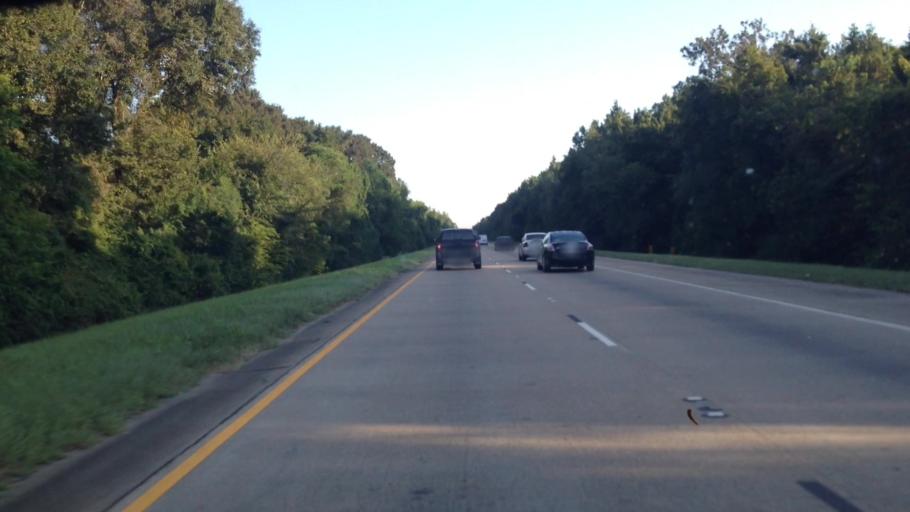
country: US
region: Louisiana
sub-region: Ascension Parish
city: Prairieville
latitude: 30.2866
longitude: -90.9897
